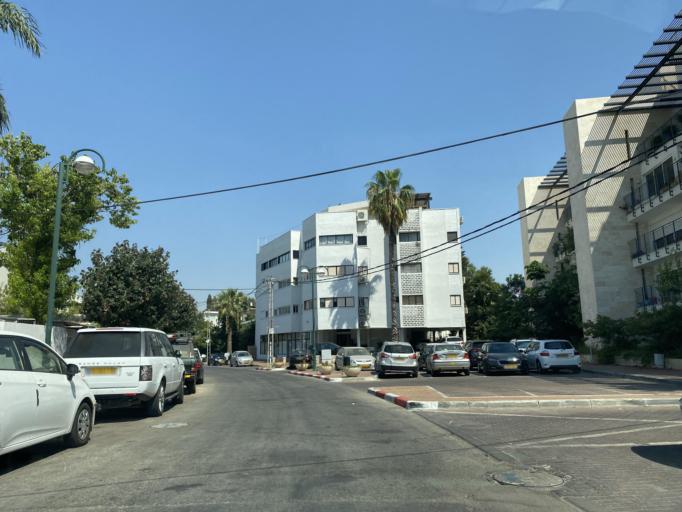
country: IL
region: Tel Aviv
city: Ramat HaSharon
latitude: 32.1328
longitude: 34.8385
